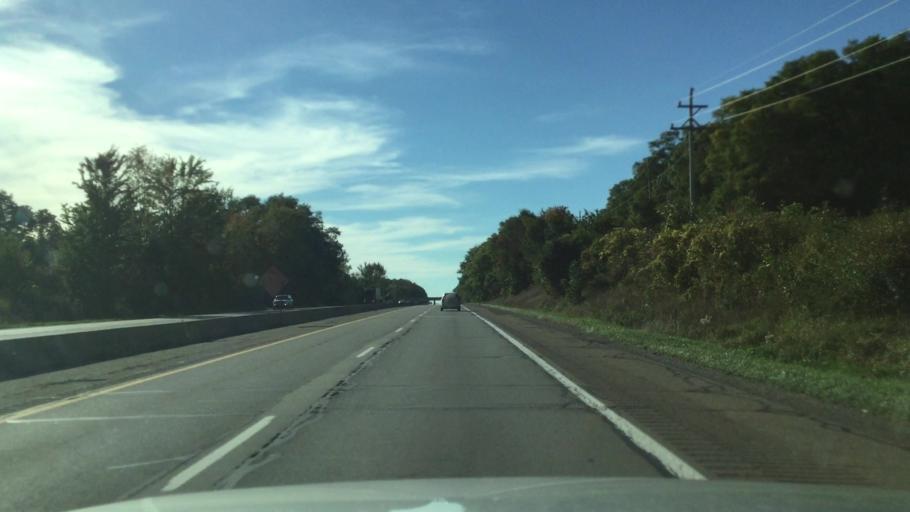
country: US
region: Michigan
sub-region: Jackson County
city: Spring Arbor
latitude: 42.2691
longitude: -84.5103
